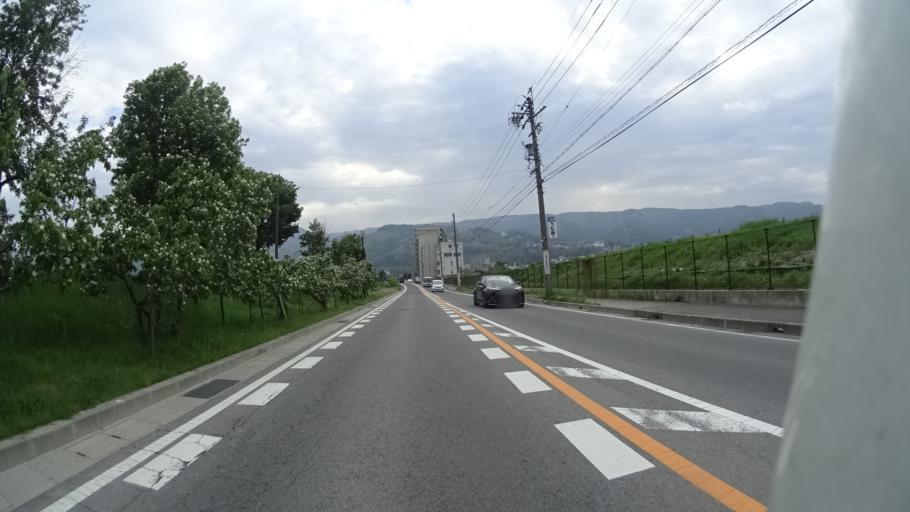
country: JP
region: Nagano
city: Suwa
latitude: 36.0444
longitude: 138.1069
